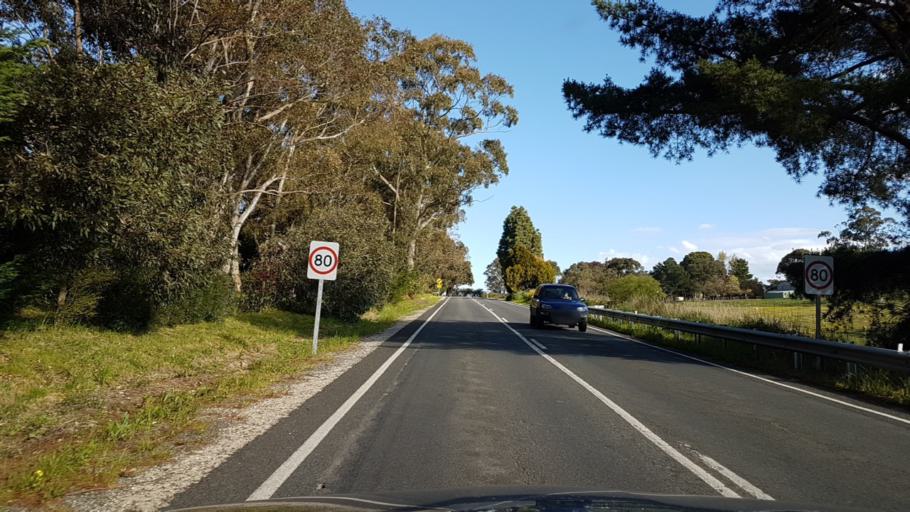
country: AU
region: South Australia
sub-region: Adelaide Hills
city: Lobethal
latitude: -34.8760
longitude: 138.8909
